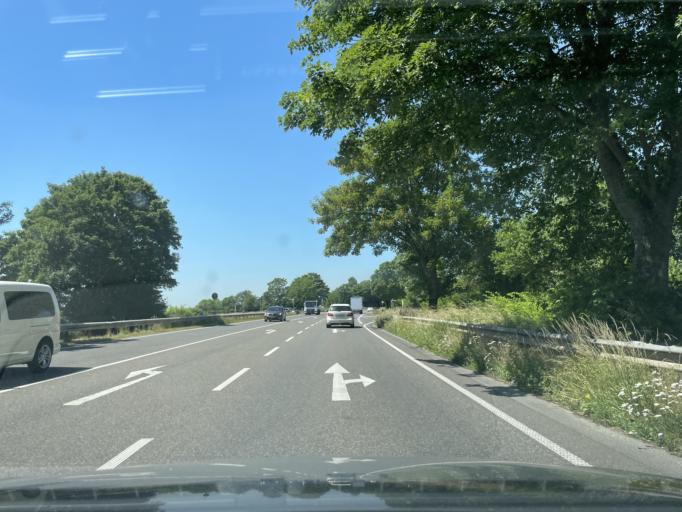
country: DE
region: North Rhine-Westphalia
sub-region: Regierungsbezirk Dusseldorf
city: Korschenbroich
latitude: 51.2190
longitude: 6.5113
